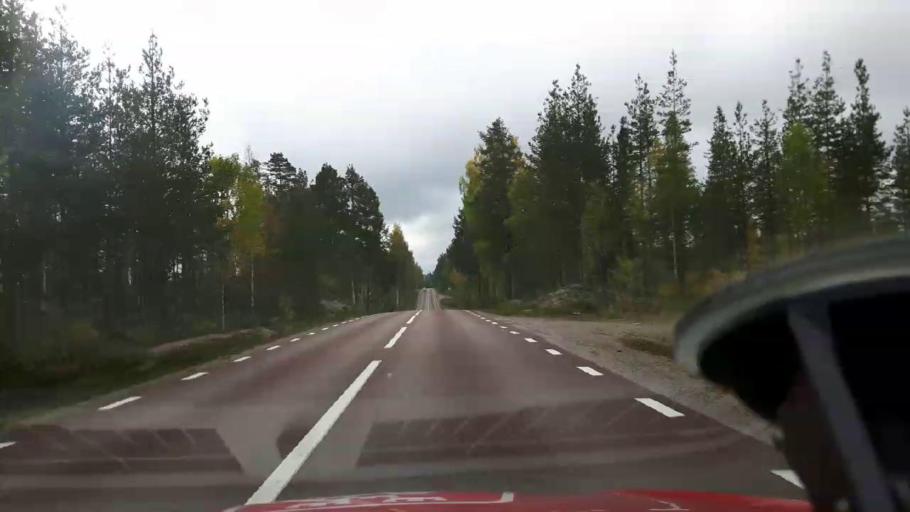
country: SE
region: Jaemtland
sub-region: Harjedalens Kommun
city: Sveg
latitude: 62.2078
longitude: 14.8463
